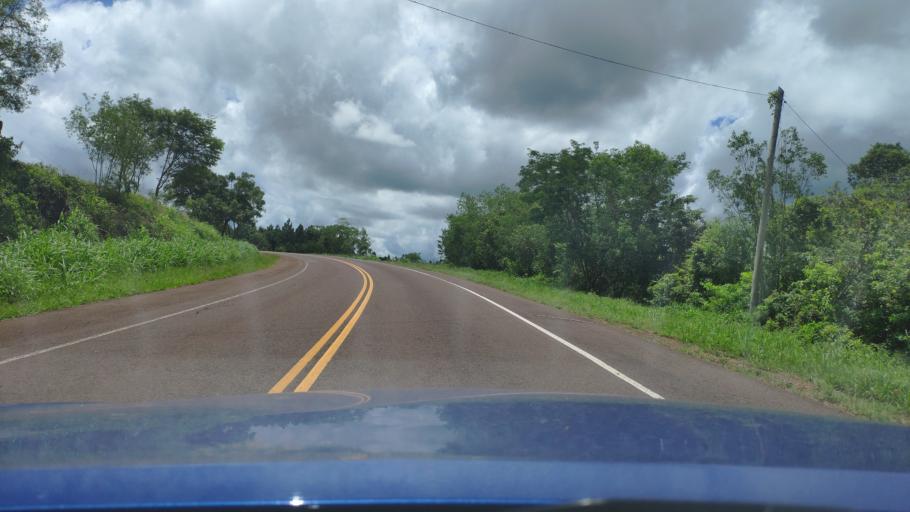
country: AR
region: Misiones
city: Dos Arroyos
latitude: -27.7541
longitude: -55.2456
